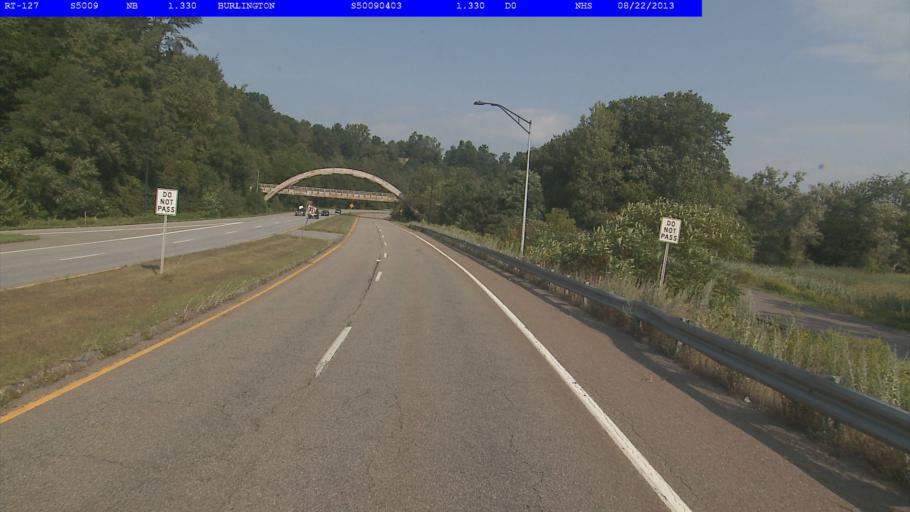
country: US
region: Vermont
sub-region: Chittenden County
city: Burlington
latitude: 44.5043
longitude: -73.2315
